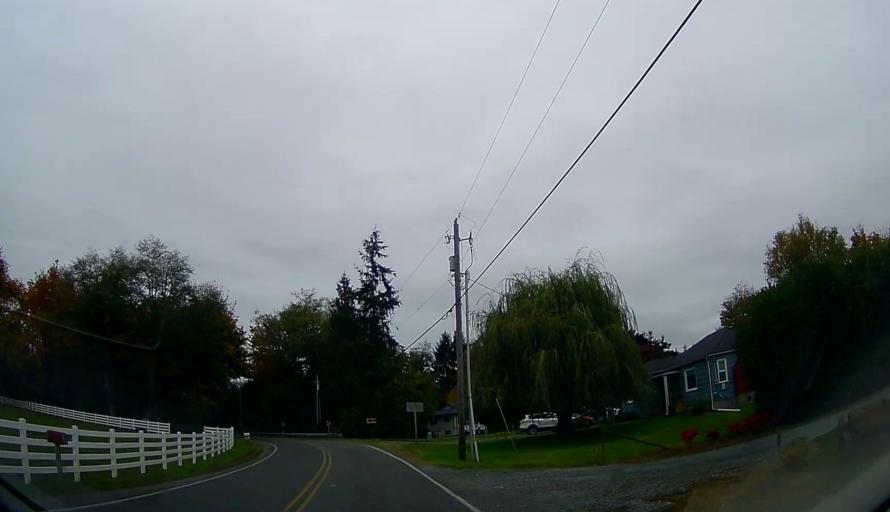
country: US
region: Washington
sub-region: Skagit County
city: Sedro-Woolley
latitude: 48.5042
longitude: -122.1977
